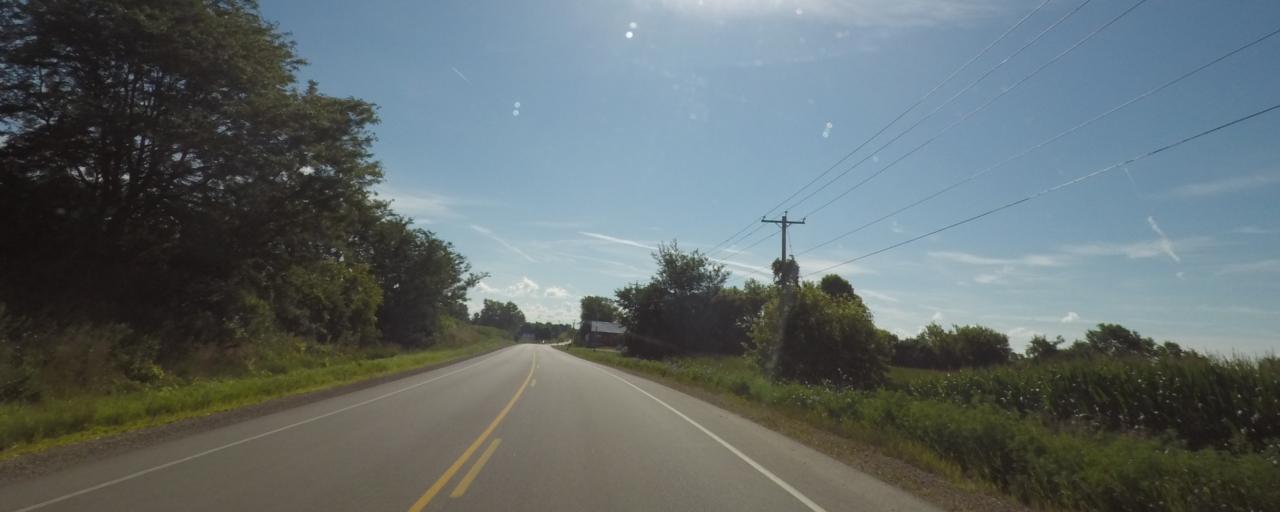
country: US
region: Wisconsin
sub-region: Jefferson County
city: Johnson Creek
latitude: 43.0758
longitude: -88.7435
